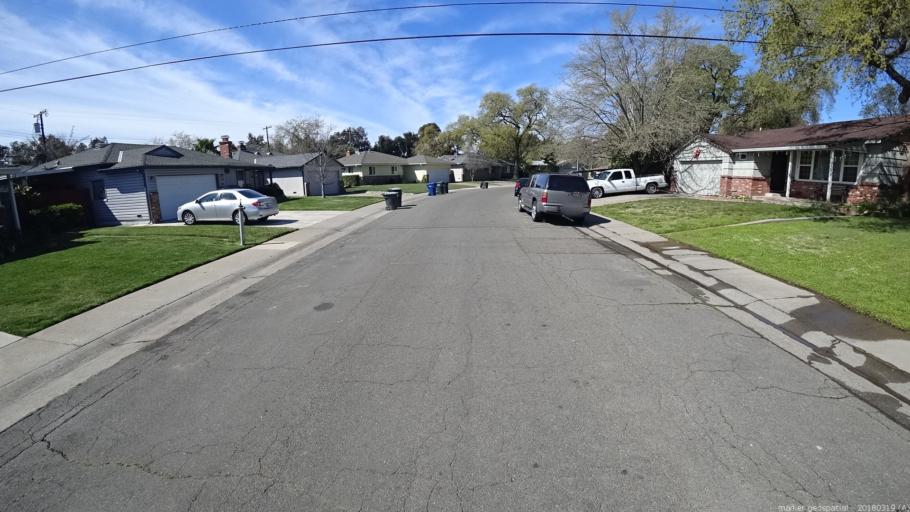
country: US
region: California
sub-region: Sacramento County
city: Parkway
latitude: 38.5116
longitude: -121.4565
